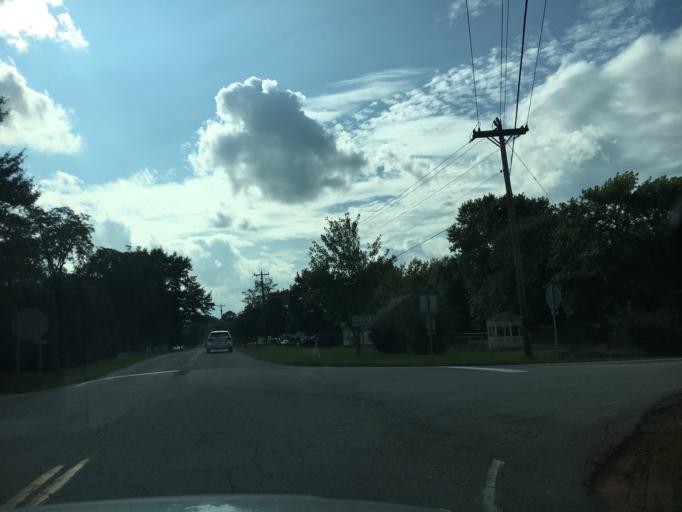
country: US
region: South Carolina
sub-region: Greenville County
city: Taylors
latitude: 34.9782
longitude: -82.2937
